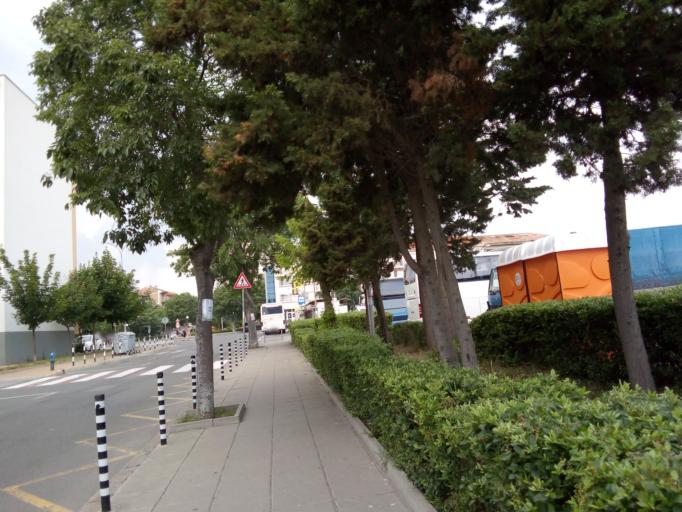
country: BG
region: Burgas
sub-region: Obshtina Pomorie
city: Pomorie
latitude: 42.5581
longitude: 27.6427
